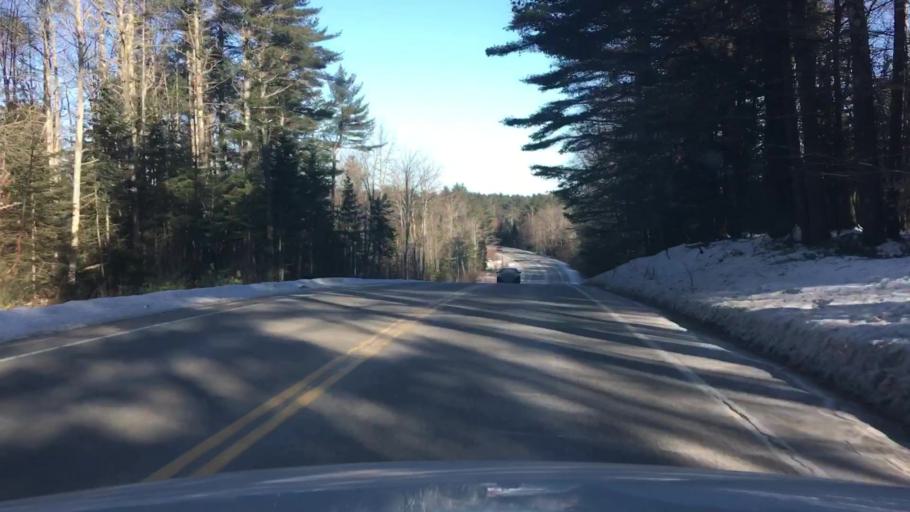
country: US
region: Maine
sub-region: Androscoggin County
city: Lisbon Falls
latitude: 43.9525
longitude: -70.1211
